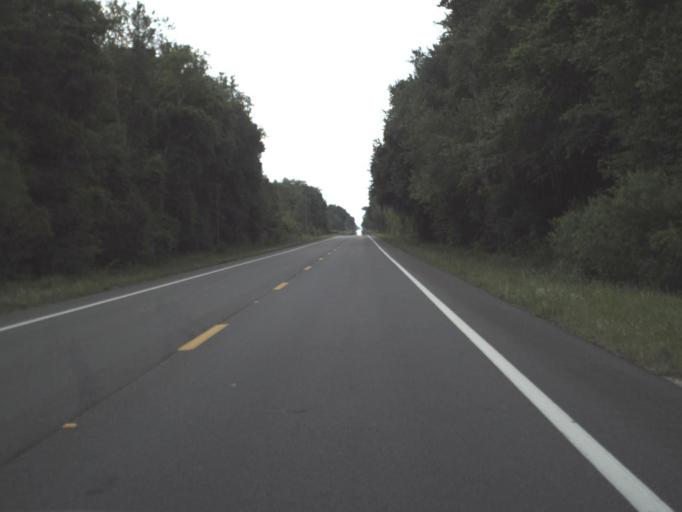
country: US
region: Florida
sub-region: Columbia County
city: Five Points
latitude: 30.4511
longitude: -82.6489
